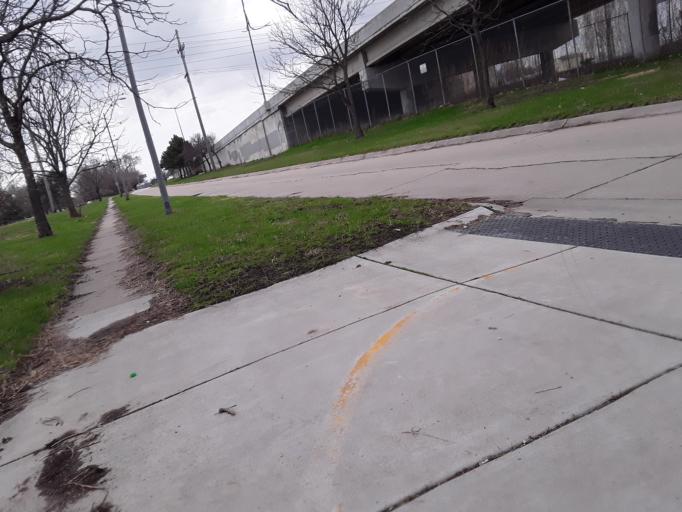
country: US
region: Nebraska
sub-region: Lancaster County
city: Lincoln
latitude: 40.8351
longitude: -96.6818
